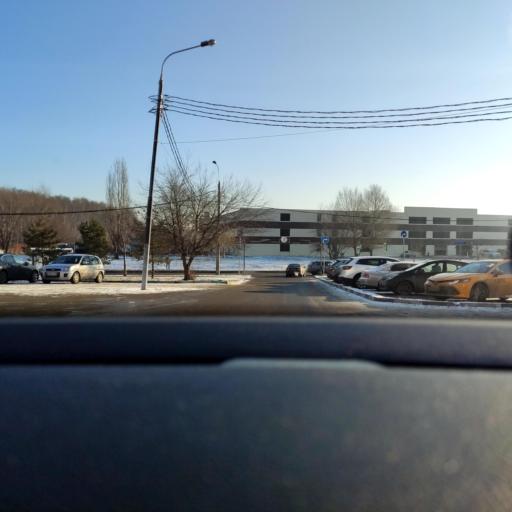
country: RU
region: Moskovskaya
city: Reutov
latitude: 55.7342
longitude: 37.8617
